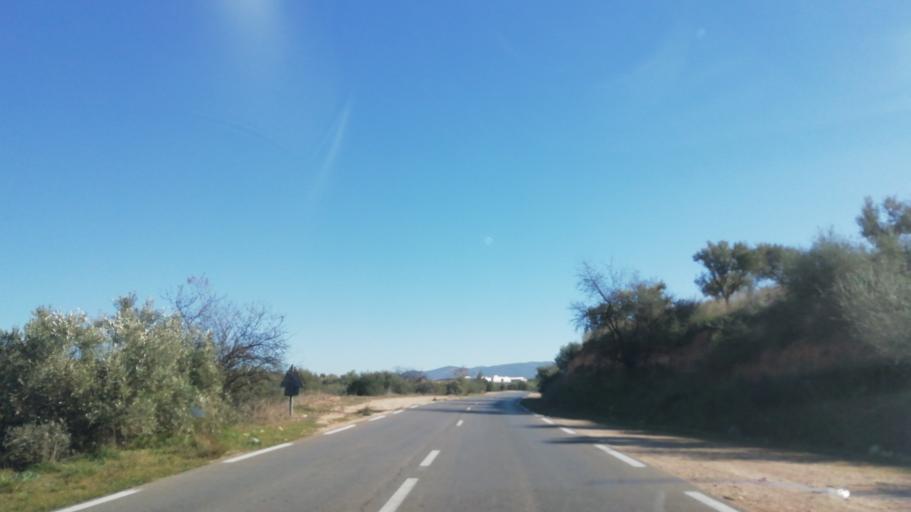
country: DZ
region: Tlemcen
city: Beni Mester
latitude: 34.8262
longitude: -1.5732
